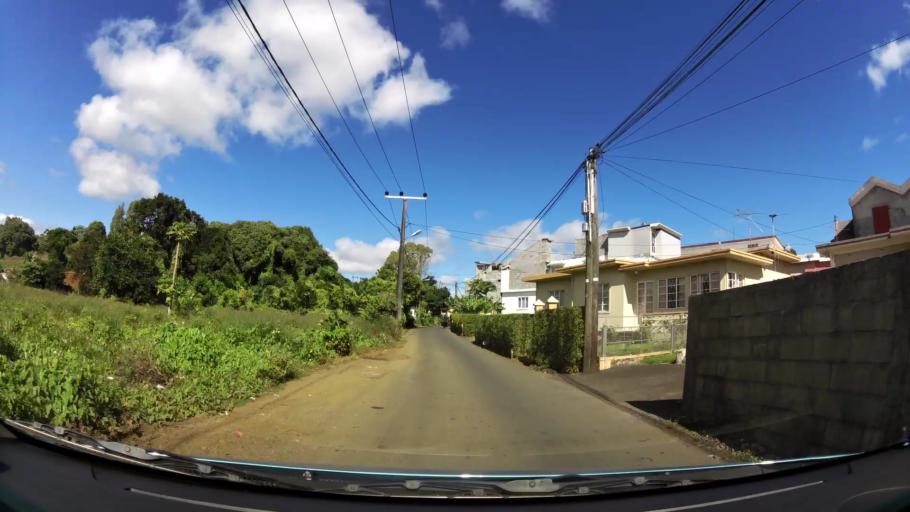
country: MU
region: Plaines Wilhems
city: Vacoas
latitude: -20.3141
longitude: 57.4921
